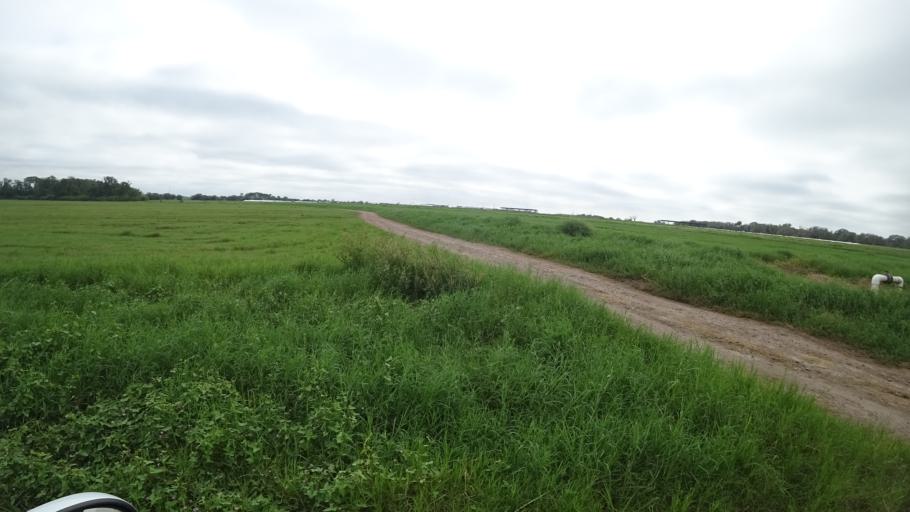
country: US
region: Florida
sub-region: Sarasota County
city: Warm Mineral Springs
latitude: 27.3244
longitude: -82.1343
